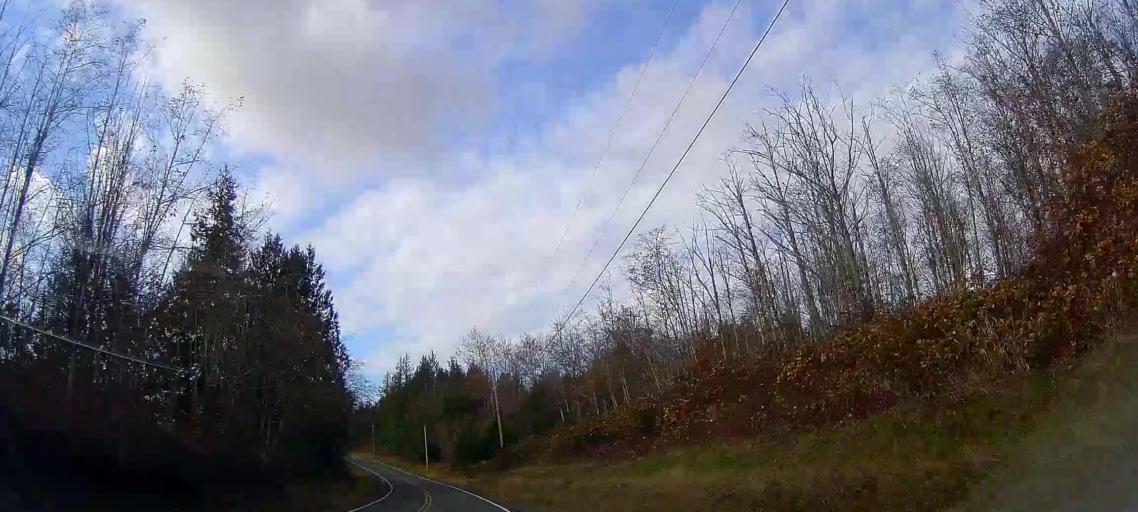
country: US
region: Washington
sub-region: Skagit County
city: Big Lake
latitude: 48.4165
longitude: -122.2265
